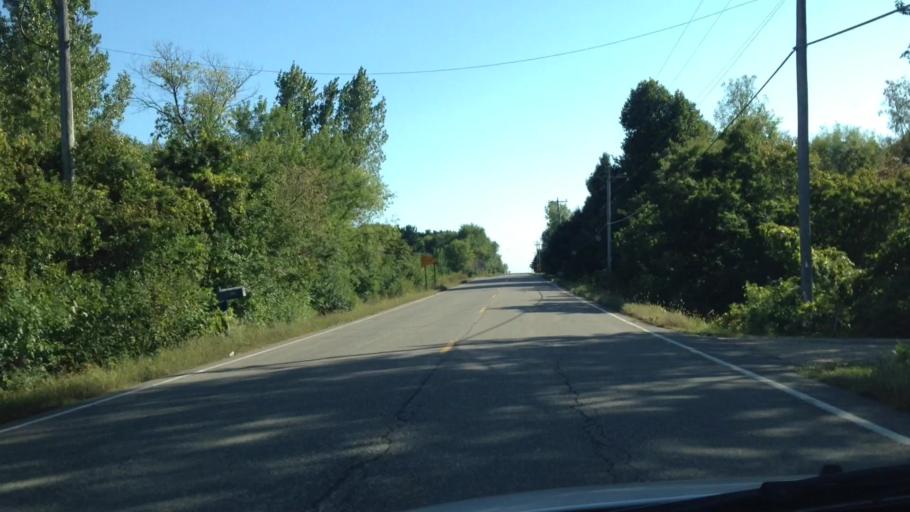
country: US
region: Minnesota
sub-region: Washington County
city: Stillwater
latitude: 45.0911
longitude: -92.8128
